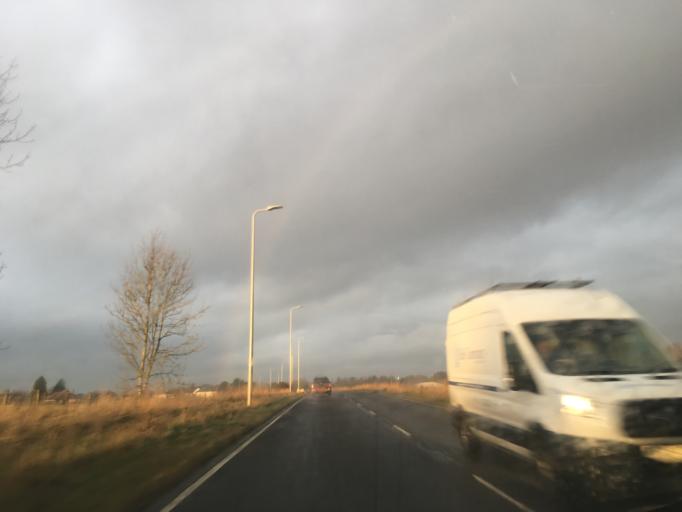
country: GB
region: Scotland
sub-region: Stirling
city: Cowie
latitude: 56.0983
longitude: -3.8345
